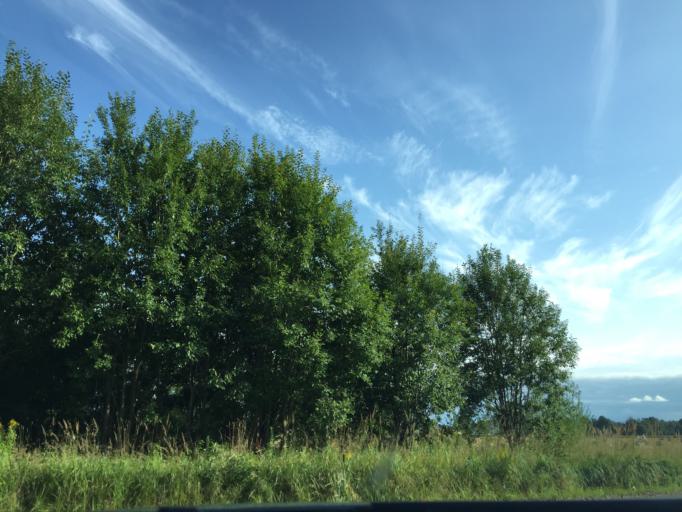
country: LV
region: Kegums
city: Kegums
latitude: 56.8226
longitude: 24.7541
